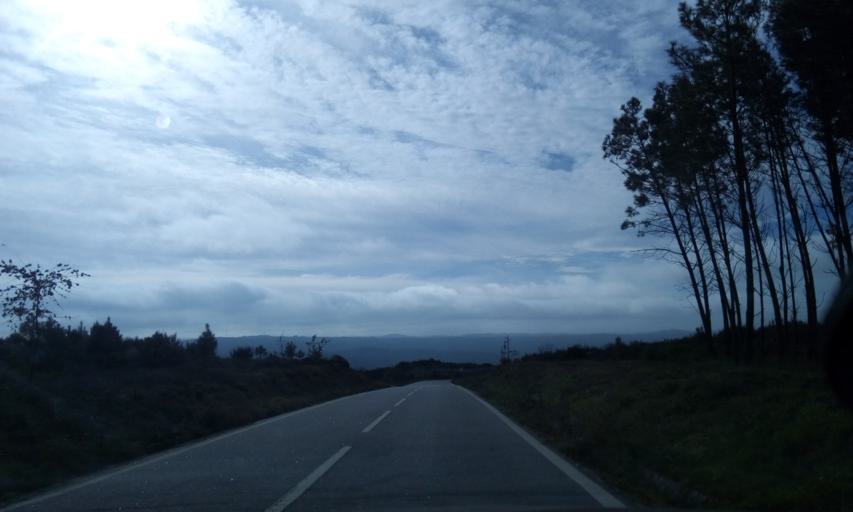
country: PT
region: Guarda
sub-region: Aguiar da Beira
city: Aguiar da Beira
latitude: 40.7539
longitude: -7.5442
